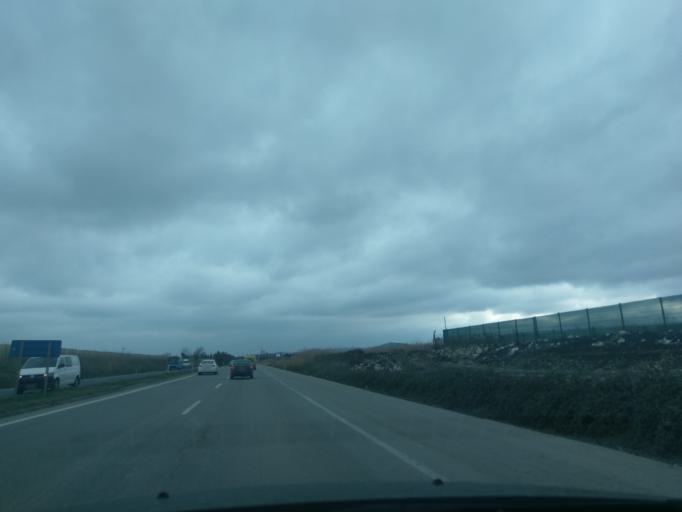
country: TR
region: Istanbul
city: Muratbey
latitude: 41.1051
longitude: 28.5065
